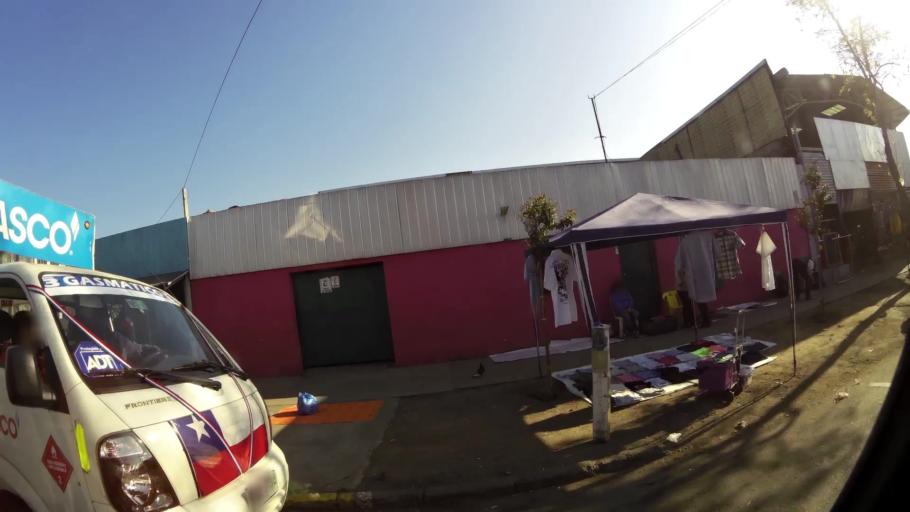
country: CL
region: Santiago Metropolitan
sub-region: Provincia de Santiago
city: Santiago
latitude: -33.4736
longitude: -70.6395
